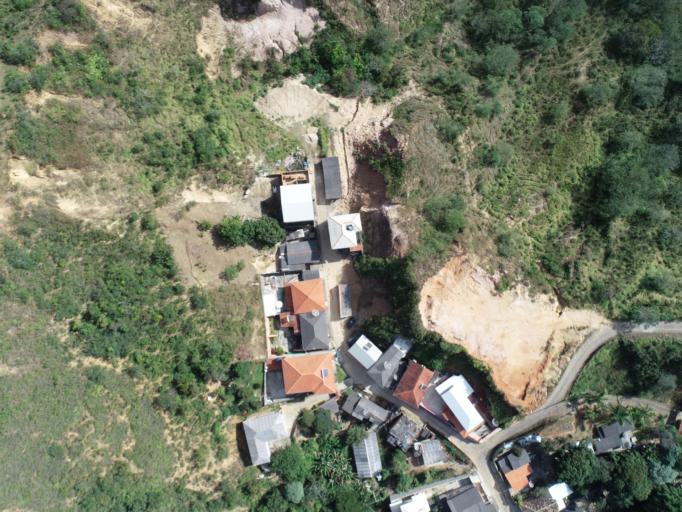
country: BR
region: Minas Gerais
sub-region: Tiradentes
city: Tiradentes
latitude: -21.0583
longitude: -44.0832
